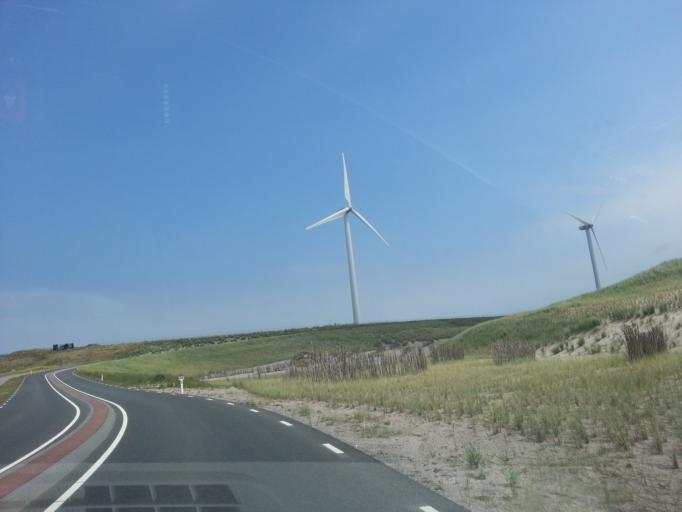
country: NL
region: South Holland
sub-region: Gemeente Goeree-Overflakkee
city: Goedereede
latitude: 51.9223
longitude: 3.9866
